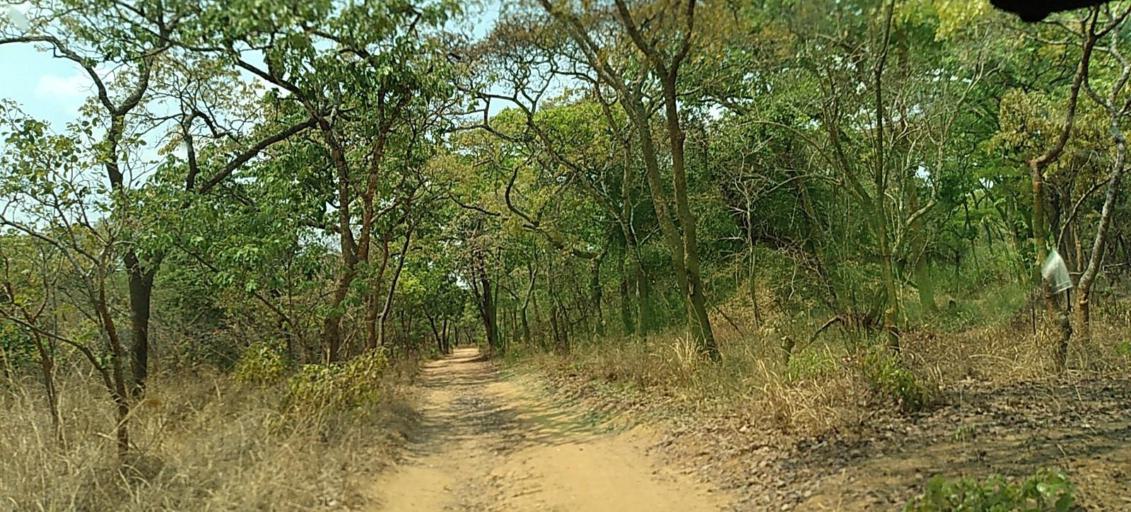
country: ZM
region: North-Western
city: Kabompo
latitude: -13.6509
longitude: 24.3742
